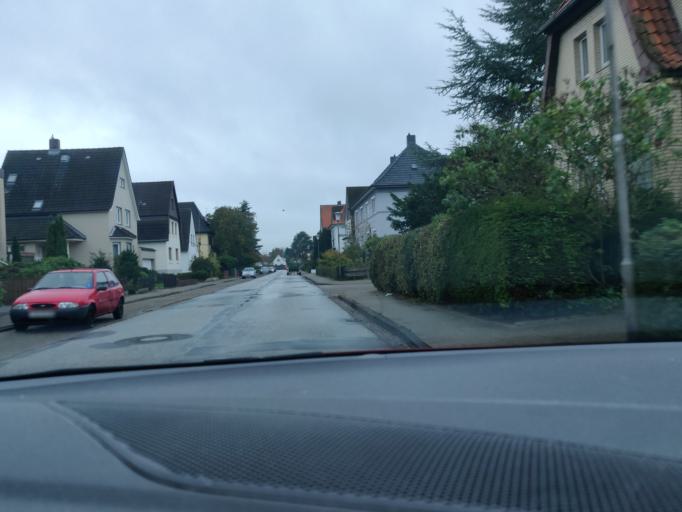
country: DE
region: Lower Saxony
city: Cuxhaven
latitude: 53.8758
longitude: 8.6841
